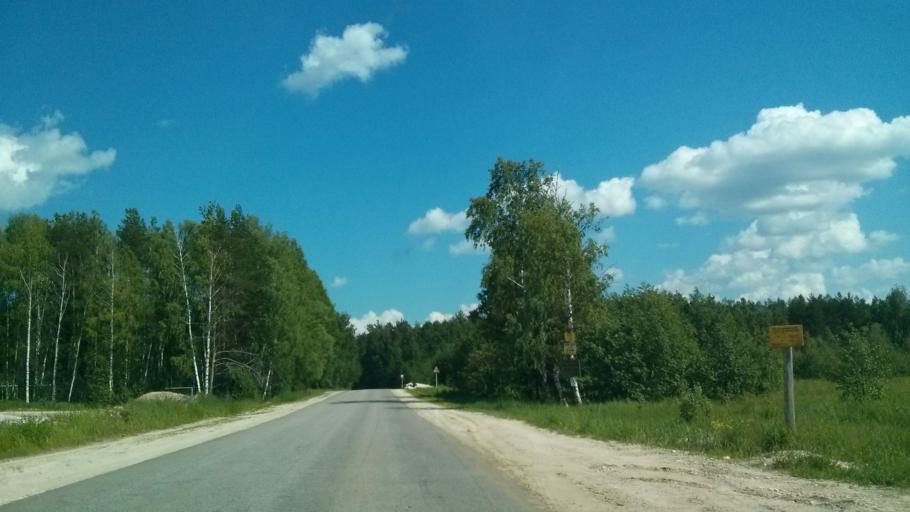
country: RU
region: Vladimir
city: Melenki
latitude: 55.3344
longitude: 41.6673
